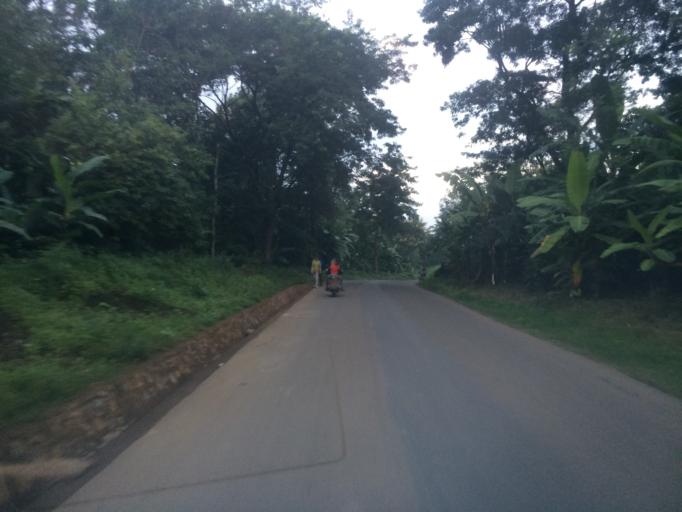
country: TZ
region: Arusha
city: Nkoaranga
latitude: -3.3513
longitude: 36.8146
